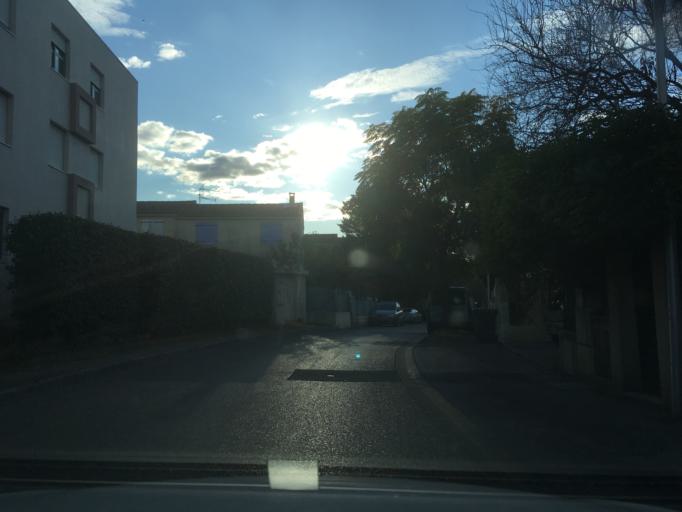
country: FR
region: Languedoc-Roussillon
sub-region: Departement de l'Herault
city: Saint-Jean-de-Vedas
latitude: 43.5932
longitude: 3.8407
